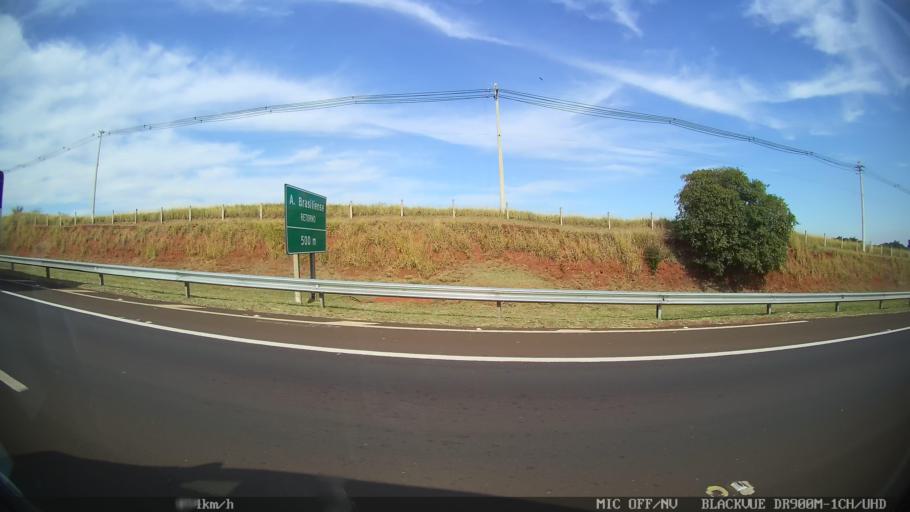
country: BR
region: Sao Paulo
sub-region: Americo Brasiliense
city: Americo Brasiliense
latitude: -21.7790
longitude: -48.1076
